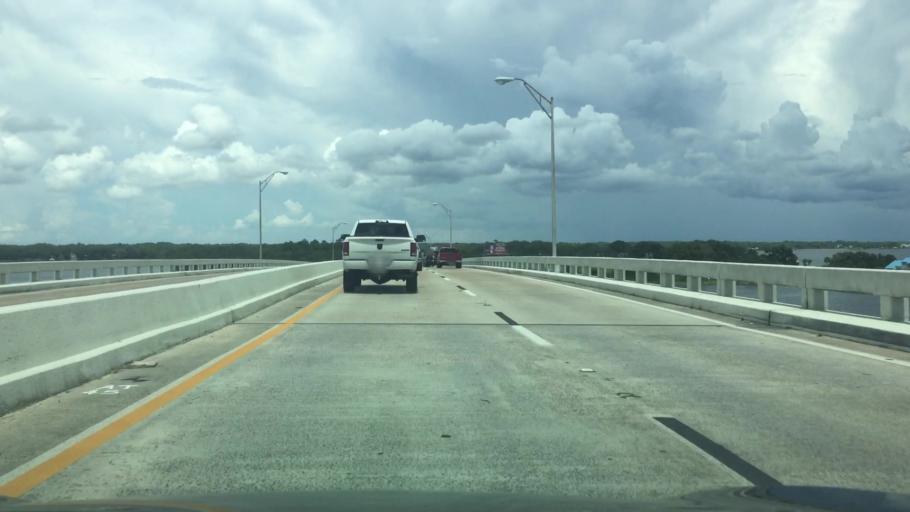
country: US
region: Florida
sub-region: Bay County
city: Tyndall Air Force Base
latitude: 30.1058
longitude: -85.6078
